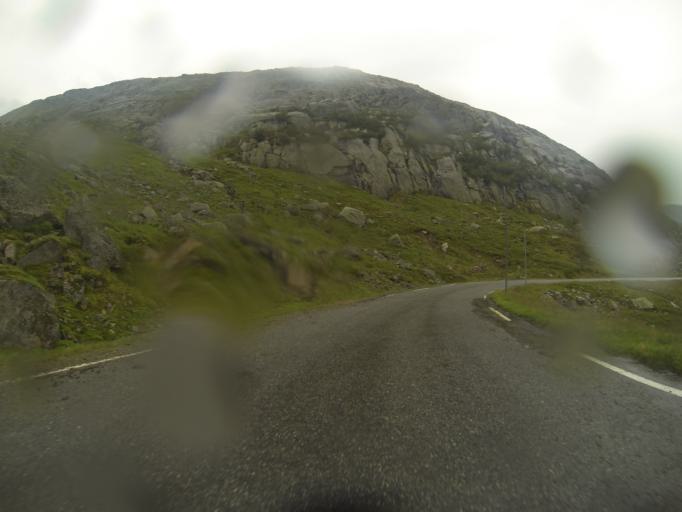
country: NO
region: Hordaland
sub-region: Odda
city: Odda
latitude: 59.7799
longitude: 6.7522
